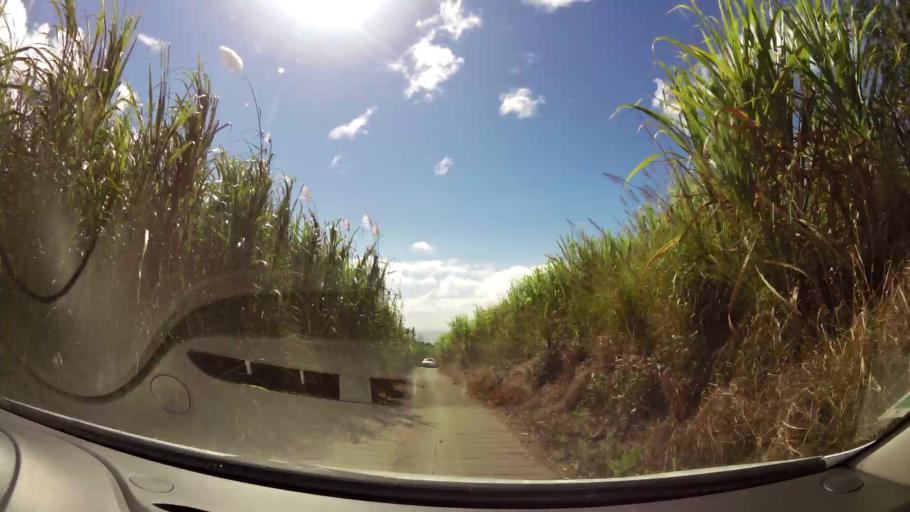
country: RE
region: Reunion
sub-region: Reunion
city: Sainte-Marie
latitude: -20.9230
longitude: 55.5071
